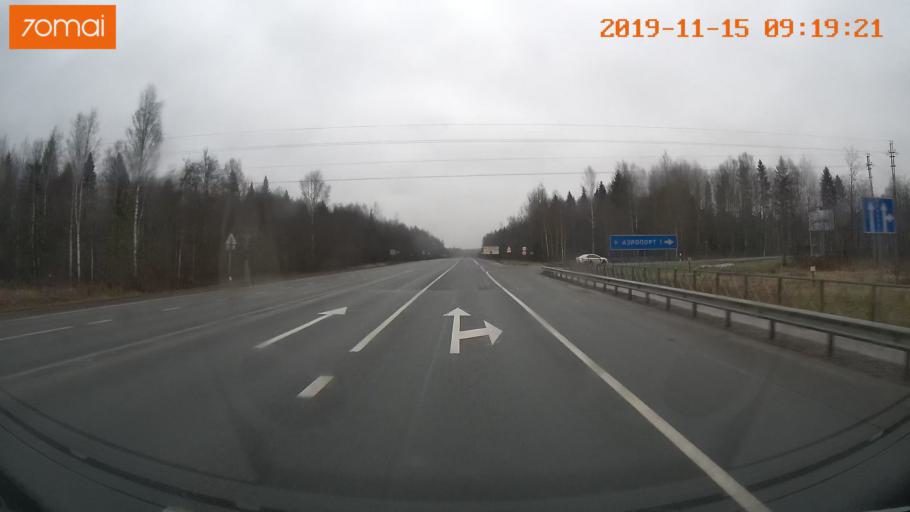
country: RU
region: Vologda
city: Tonshalovo
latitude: 59.2831
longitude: 38.0146
